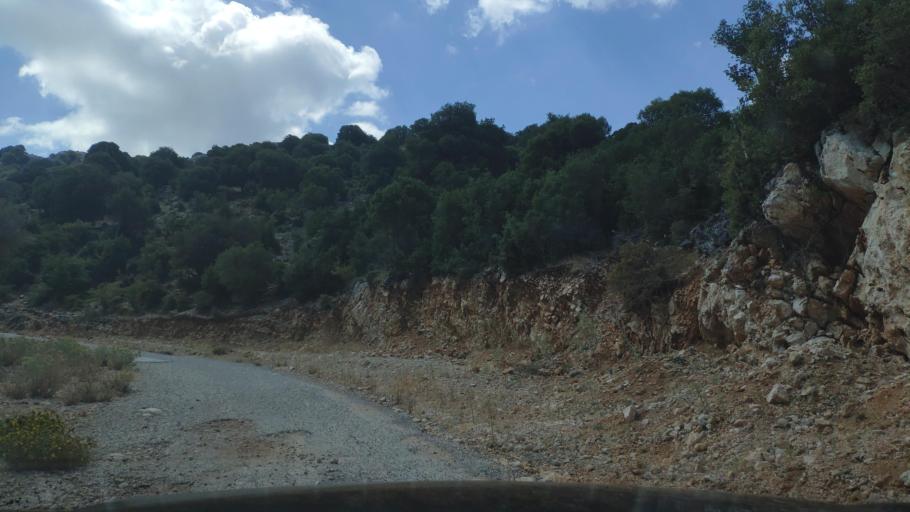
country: GR
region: West Greece
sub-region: Nomos Aitolias kai Akarnanias
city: Monastirakion
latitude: 38.7856
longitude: 20.9801
